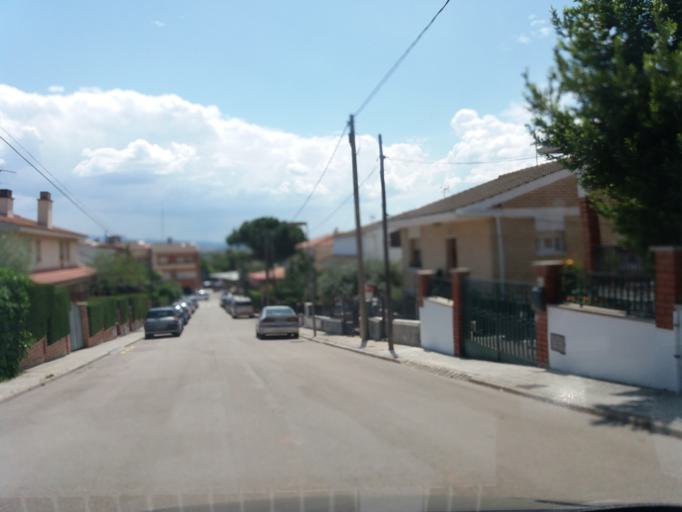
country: ES
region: Catalonia
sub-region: Provincia de Barcelona
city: Sant Joan de Vilatorrada
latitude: 41.7432
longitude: 1.8010
